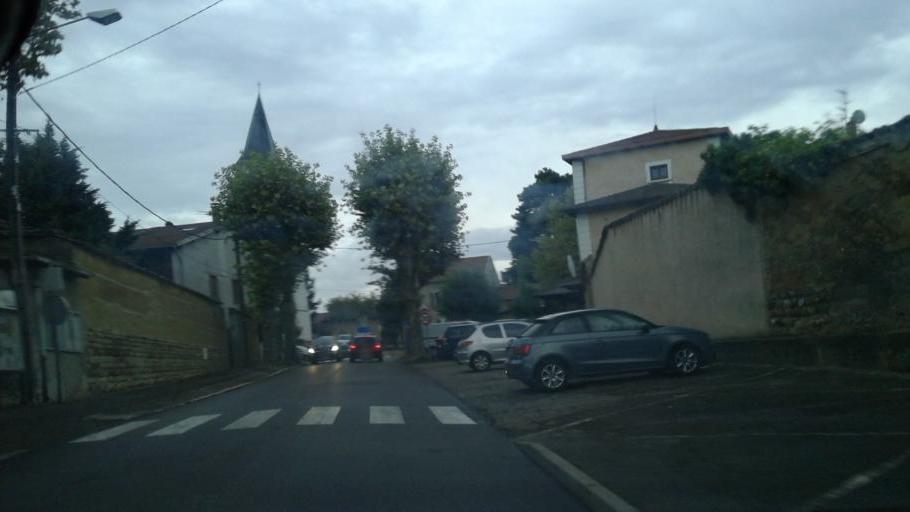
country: FR
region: Rhone-Alpes
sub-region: Departement de l'Ain
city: Miribel
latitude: 45.8296
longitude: 4.9459
